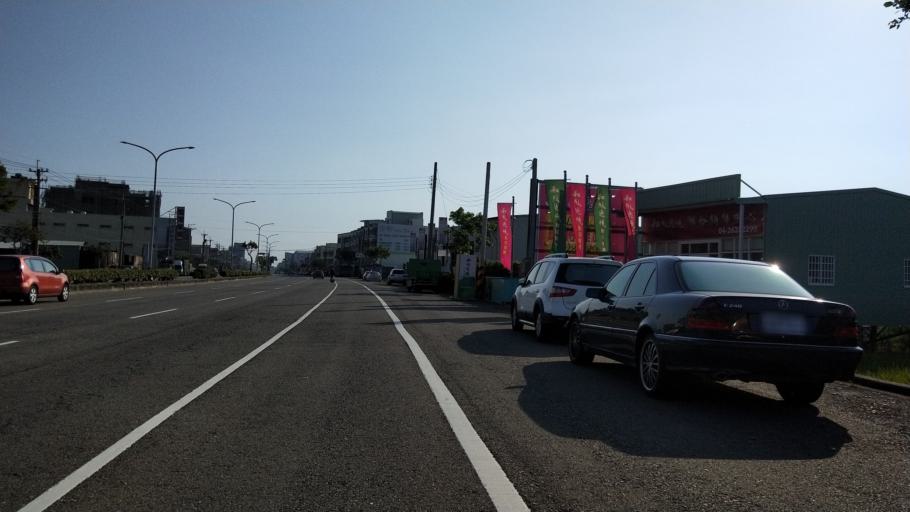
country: TW
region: Taiwan
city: Fengyuan
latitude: 24.2607
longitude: 120.5603
